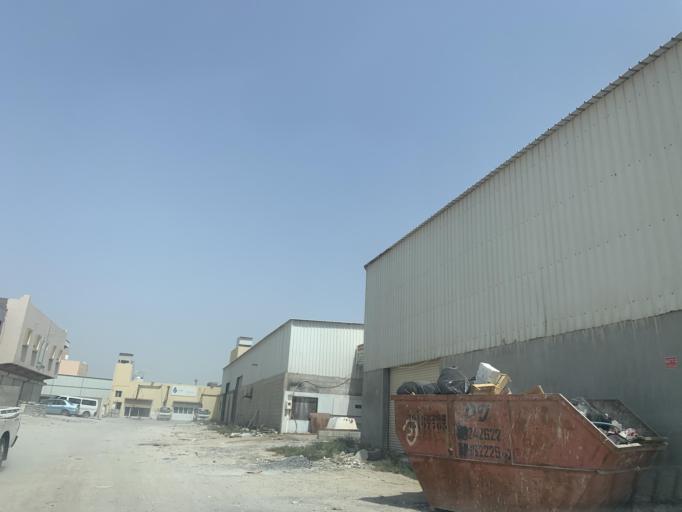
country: BH
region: Central Governorate
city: Madinat Hamad
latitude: 26.1417
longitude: 50.4854
